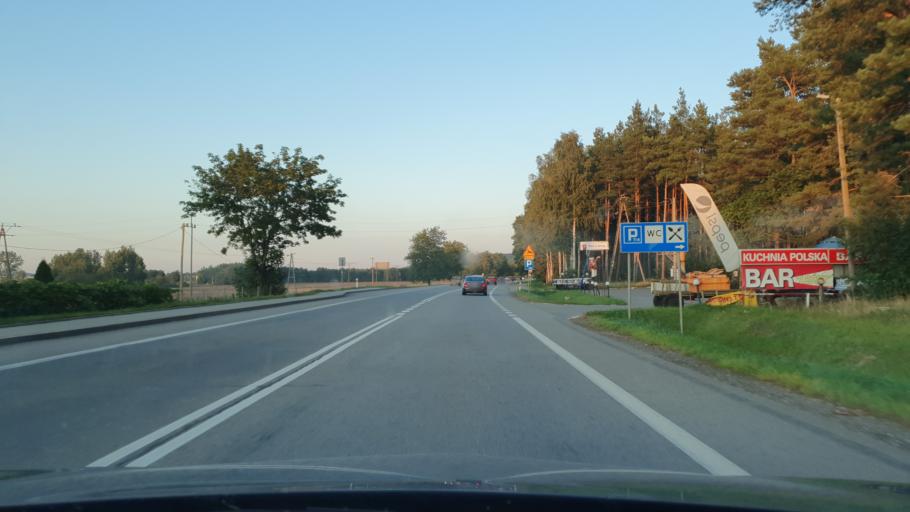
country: PL
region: Pomeranian Voivodeship
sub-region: Powiat leborski
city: Nowa Wies Leborska
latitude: 54.5050
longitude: 17.6528
